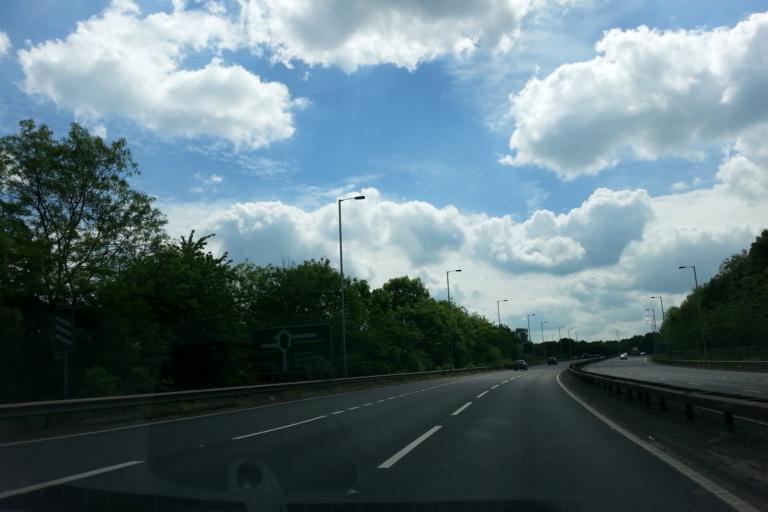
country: GB
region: England
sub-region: Peterborough
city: Peterborough
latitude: 52.5494
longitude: -0.2656
